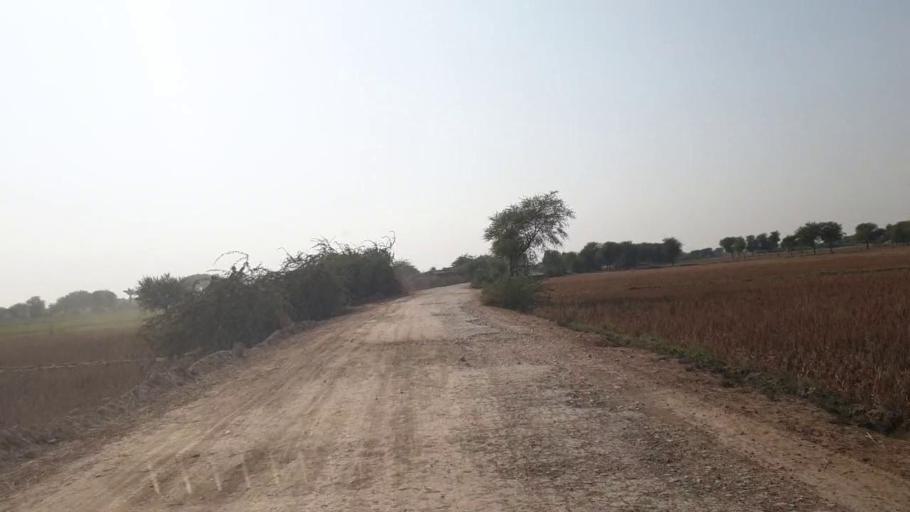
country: PK
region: Sindh
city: Matli
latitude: 24.9519
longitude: 68.6895
